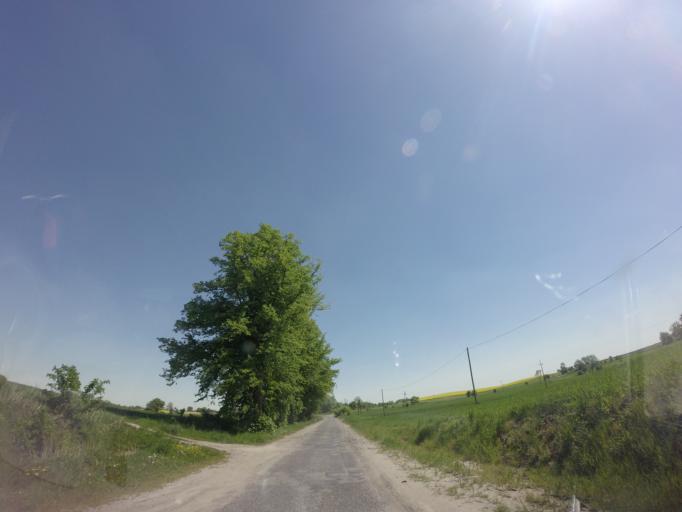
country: PL
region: West Pomeranian Voivodeship
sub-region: Powiat mysliborski
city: Nowogrodek Pomorski
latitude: 52.9086
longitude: 15.0371
